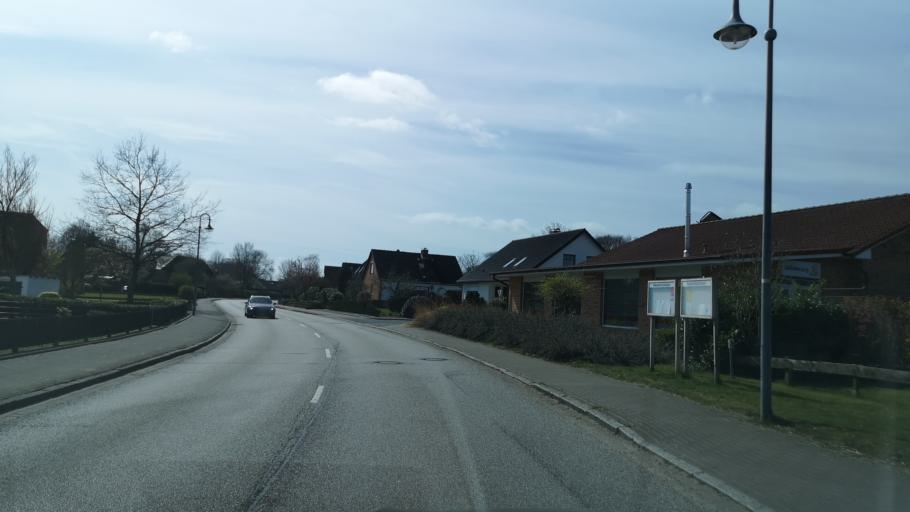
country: DE
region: Schleswig-Holstein
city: Hamdorf
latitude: 54.2301
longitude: 9.5166
